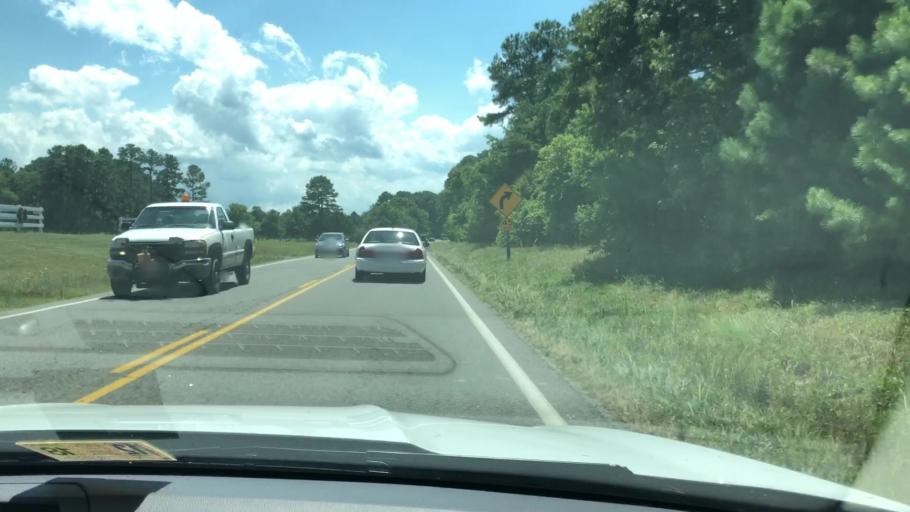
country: US
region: Virginia
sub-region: Middlesex County
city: Deltaville
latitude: 37.6019
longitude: -76.4417
